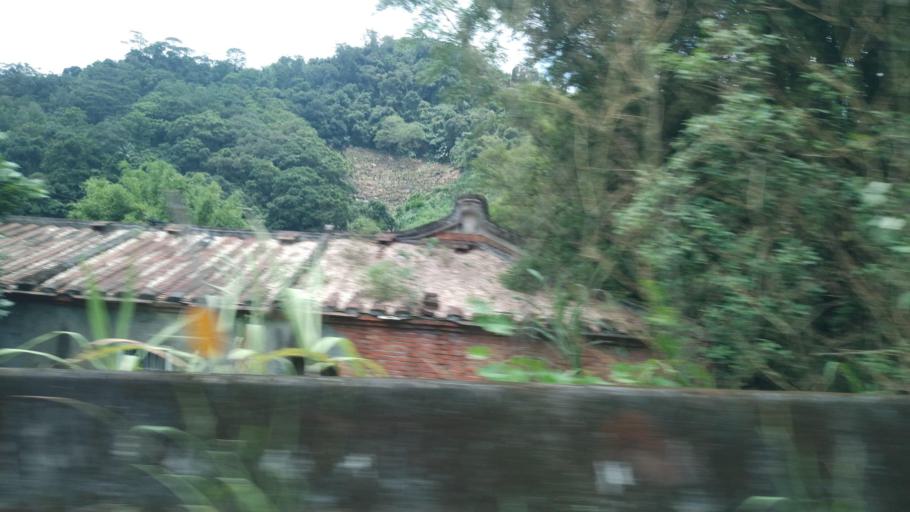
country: TW
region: Taipei
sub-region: Taipei
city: Banqiao
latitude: 24.9309
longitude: 121.4525
